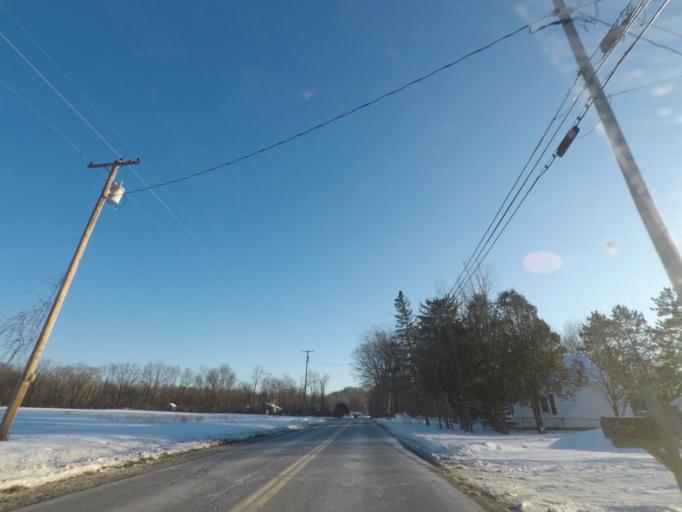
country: US
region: New York
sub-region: Saratoga County
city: Mechanicville
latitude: 42.8938
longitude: -73.6789
